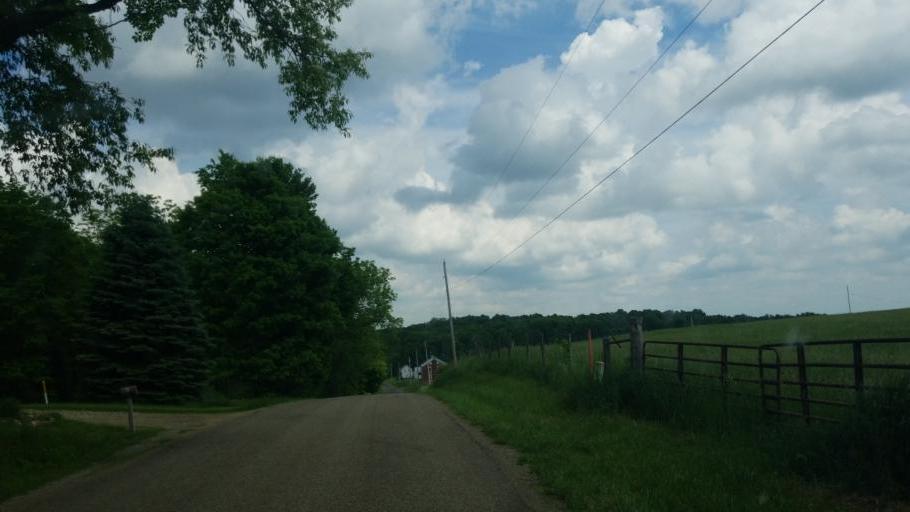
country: US
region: Ohio
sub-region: Sandusky County
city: Bellville
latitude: 40.6463
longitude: -82.4127
